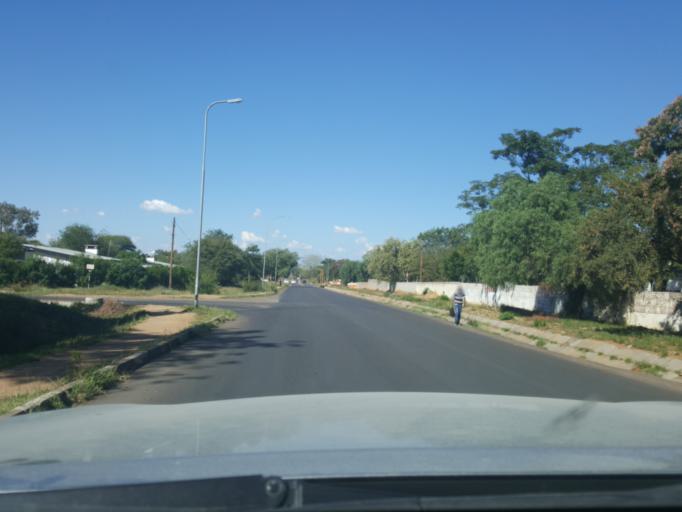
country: BW
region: South East
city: Gaborone
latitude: -24.6263
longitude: 25.9405
